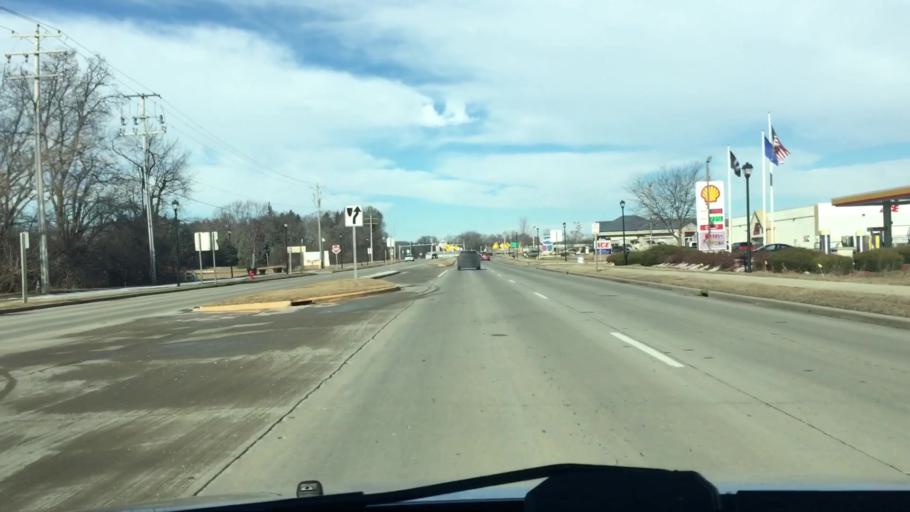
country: US
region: Wisconsin
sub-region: Waukesha County
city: Mukwonago
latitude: 42.8766
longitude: -88.3392
